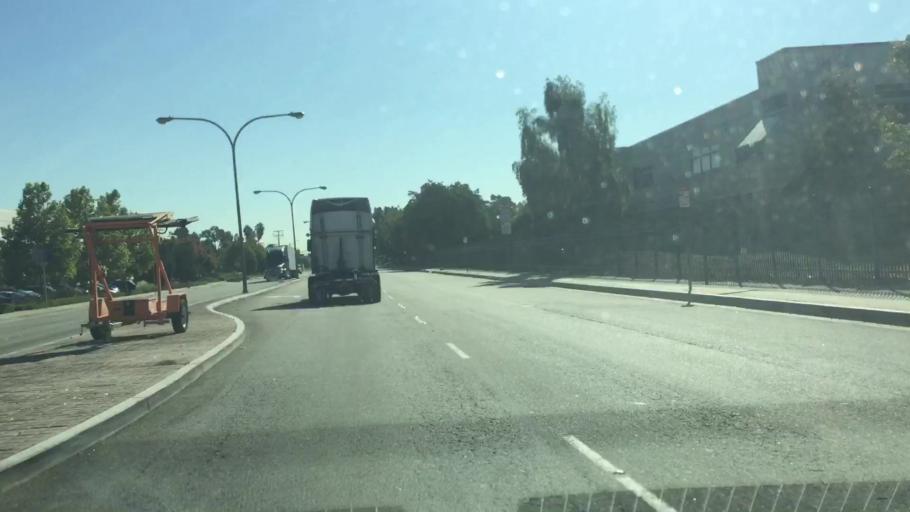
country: US
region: California
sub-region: Los Angeles County
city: Commerce
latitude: 33.9972
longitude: -118.1719
